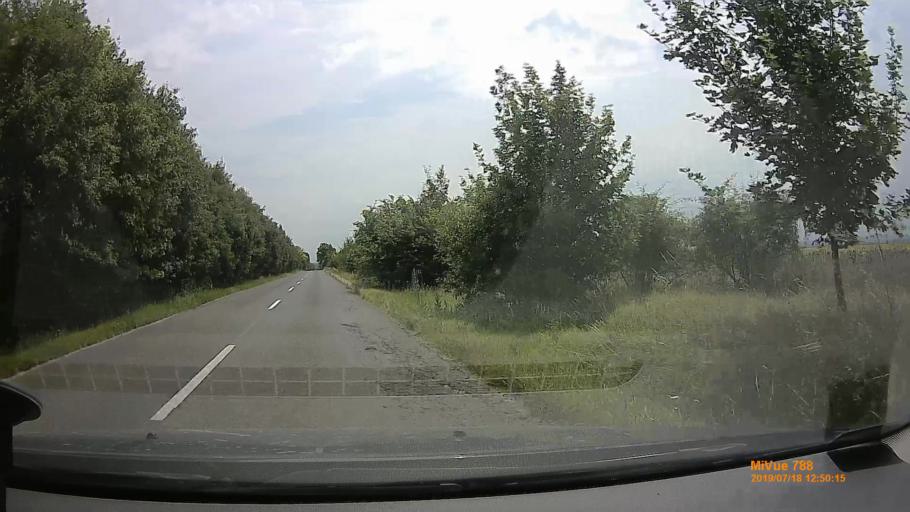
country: HU
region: Pest
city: Perbal
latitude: 47.5698
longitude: 18.7886
